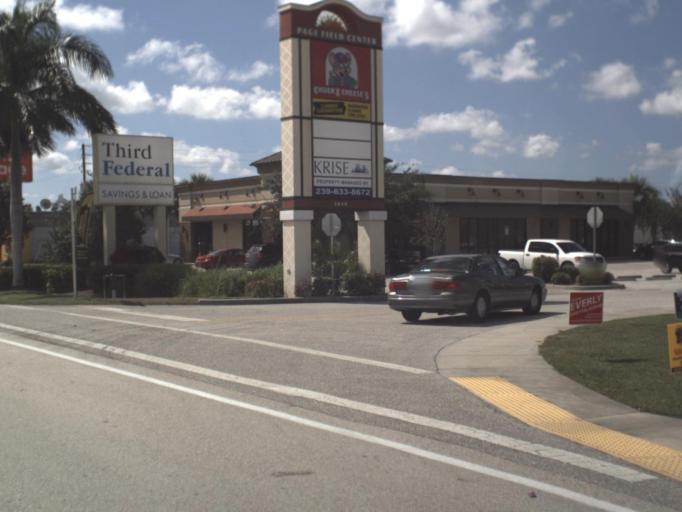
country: US
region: Florida
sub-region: Lee County
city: Pine Manor
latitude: 26.5881
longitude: -81.8720
